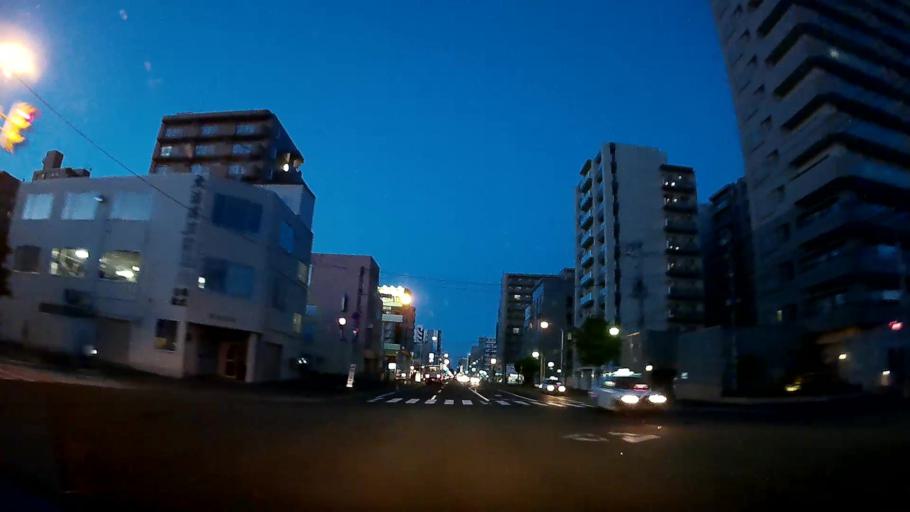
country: JP
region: Hokkaido
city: Sapporo
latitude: 43.0632
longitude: 141.3238
